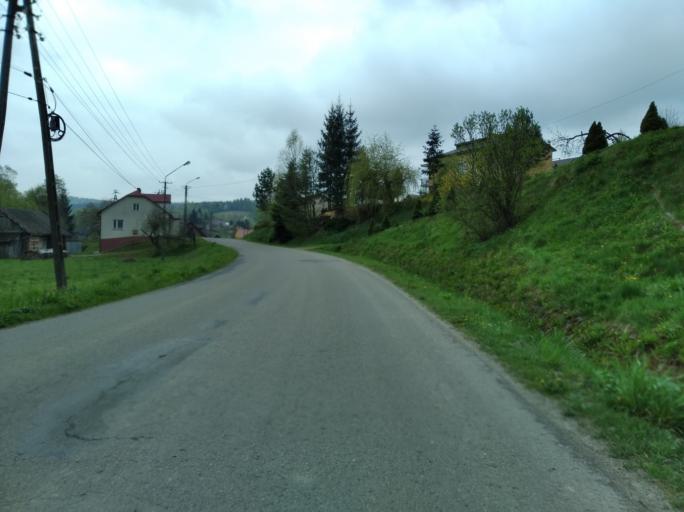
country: PL
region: Subcarpathian Voivodeship
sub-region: Powiat brzozowski
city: Jablonka
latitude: 49.7386
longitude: 22.0789
